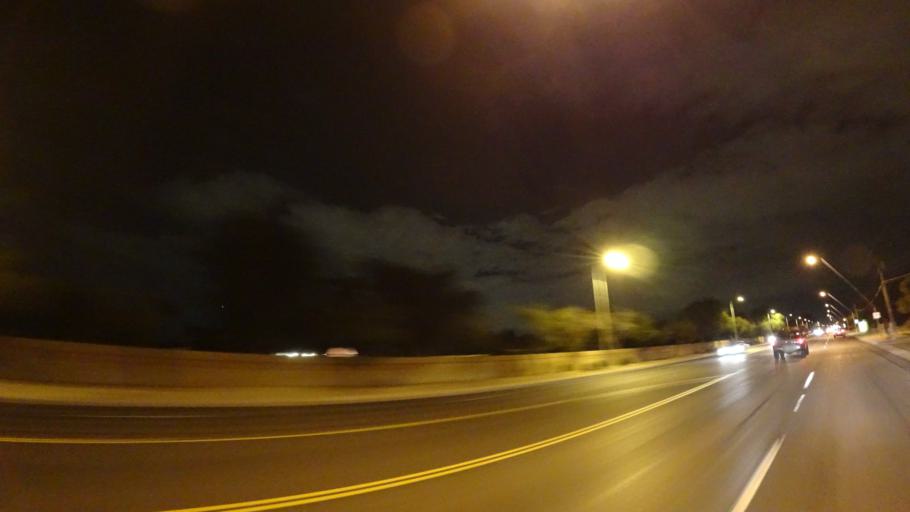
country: US
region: Arizona
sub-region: Maricopa County
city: San Carlos
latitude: 33.3425
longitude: -111.8590
